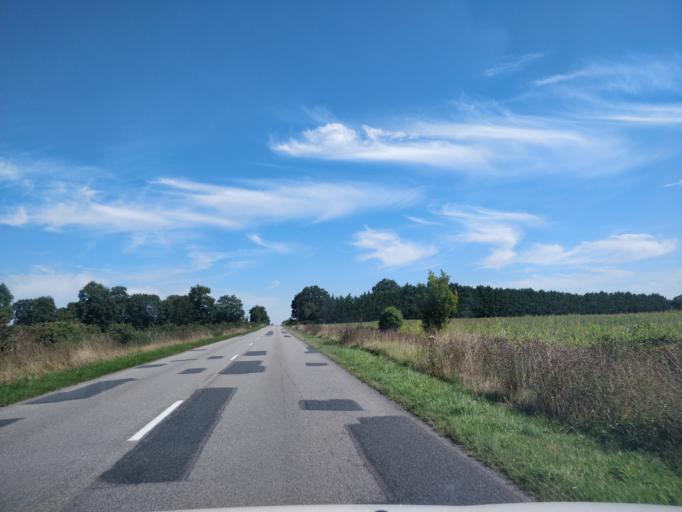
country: FR
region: Pays de la Loire
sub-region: Departement de la Loire-Atlantique
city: Plesse
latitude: 47.5781
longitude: -1.8618
